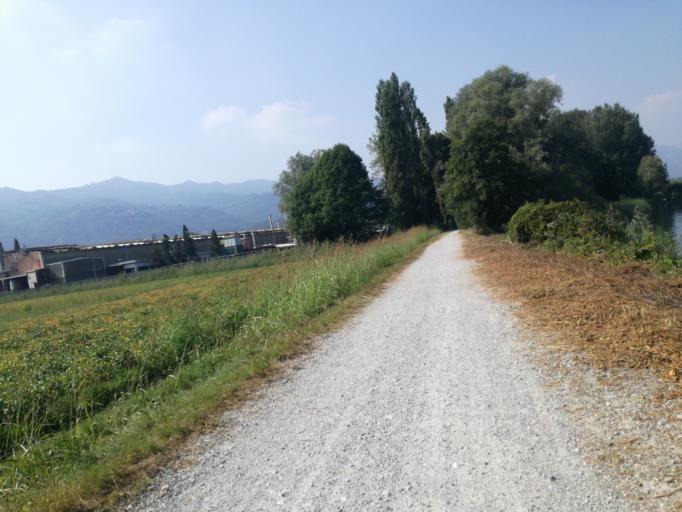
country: IT
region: Lombardy
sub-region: Provincia di Lecco
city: Brivio
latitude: 45.7536
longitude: 9.4465
